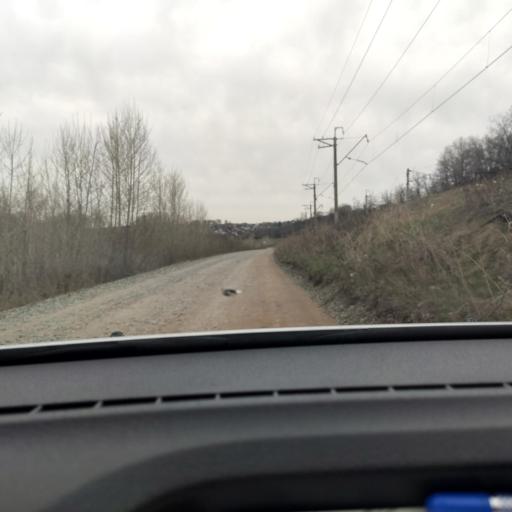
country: RU
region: Bashkortostan
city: Avdon
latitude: 54.6117
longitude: 55.6081
